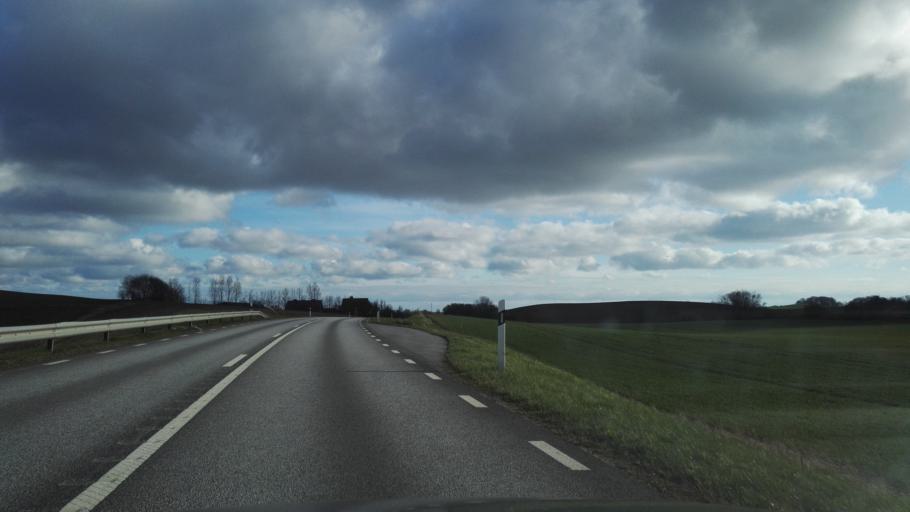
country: SE
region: Skane
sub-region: Ystads Kommun
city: Ystad
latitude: 55.4639
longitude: 13.7986
